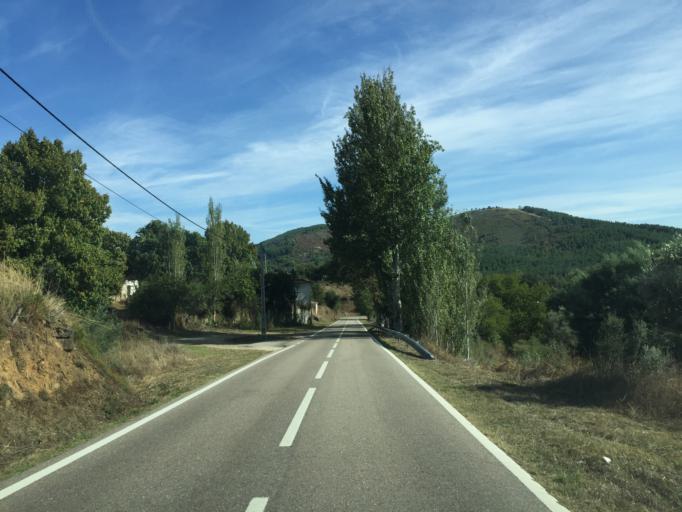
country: PT
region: Portalegre
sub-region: Marvao
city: Marvao
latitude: 39.3885
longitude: -7.3864
